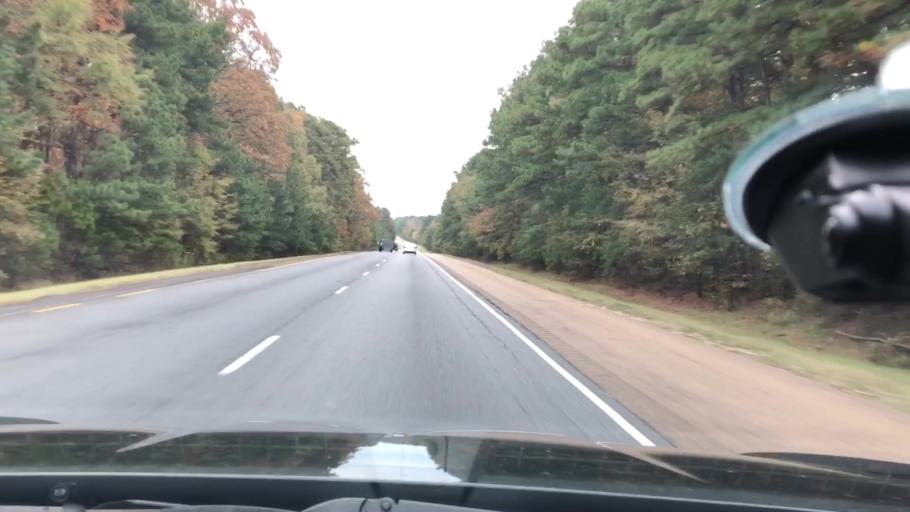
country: US
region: Arkansas
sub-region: Clark County
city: Gurdon
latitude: 33.9402
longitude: -93.2459
